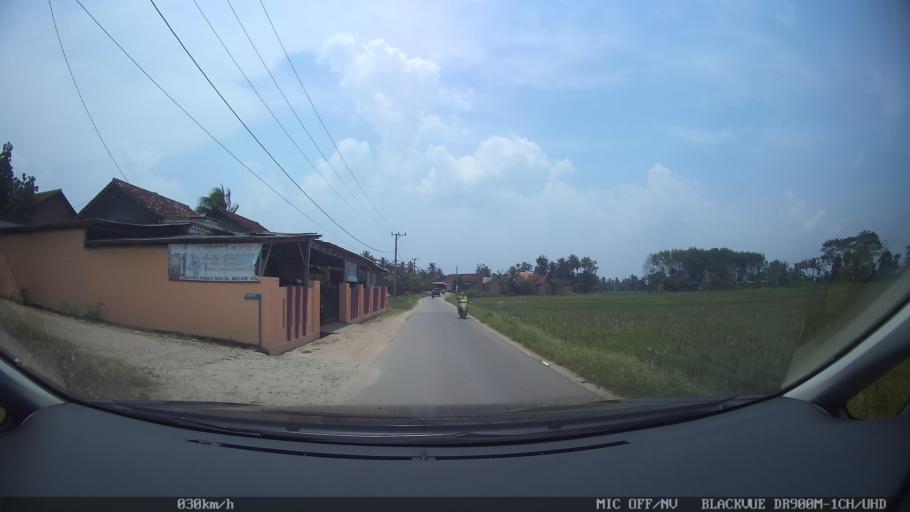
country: ID
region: Lampung
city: Kedaton
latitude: -5.3299
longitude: 105.2466
